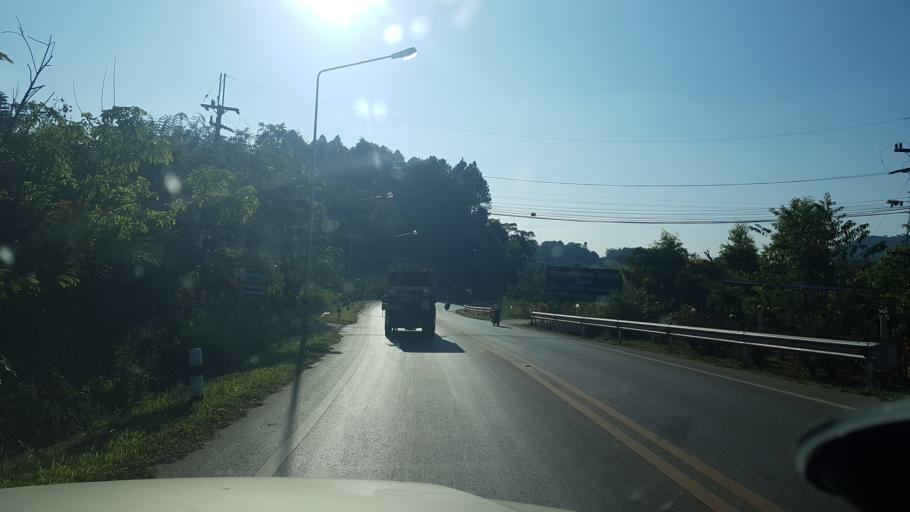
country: TH
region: Phetchabun
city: Khao Kho
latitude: 16.6482
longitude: 101.0095
